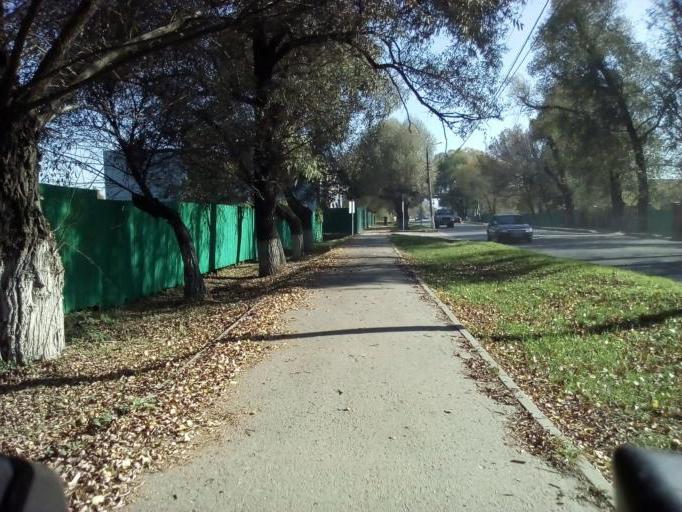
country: RU
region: Moskovskaya
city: Ramenskoye
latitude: 55.5560
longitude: 38.2641
